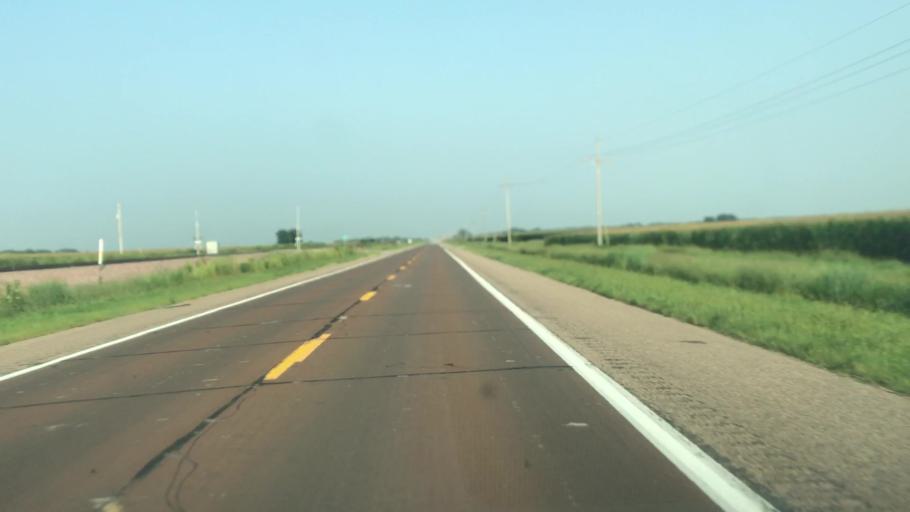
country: US
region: Nebraska
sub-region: Hall County
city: Grand Island
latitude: 40.9653
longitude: -98.4379
